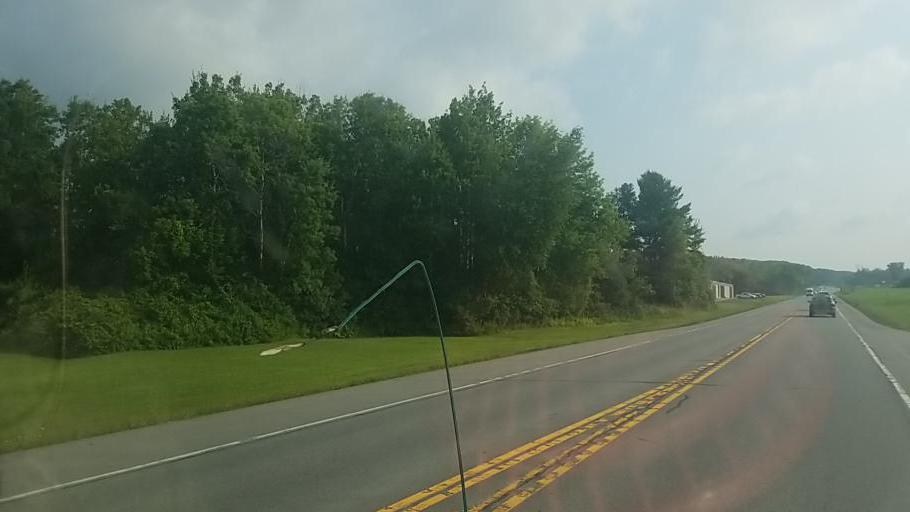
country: US
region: New York
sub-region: Fulton County
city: Gloversville
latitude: 43.0282
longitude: -74.3508
